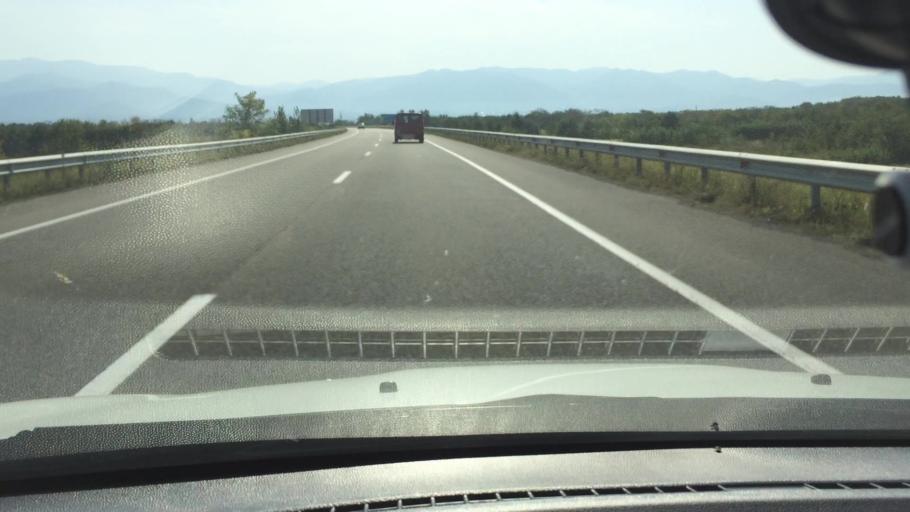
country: GE
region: Guria
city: Urek'i
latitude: 41.9129
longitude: 41.7798
